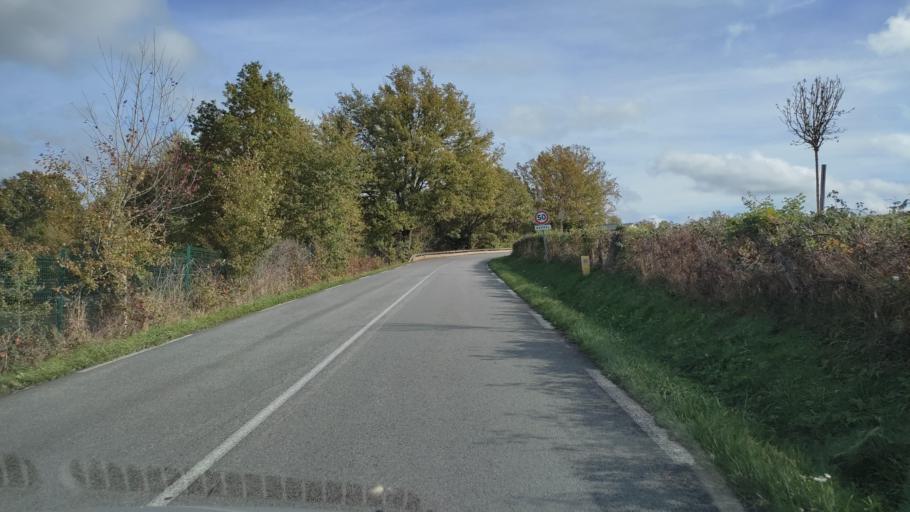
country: FR
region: Limousin
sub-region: Departement de la Haute-Vienne
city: Isle
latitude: 45.8163
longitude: 1.2133
